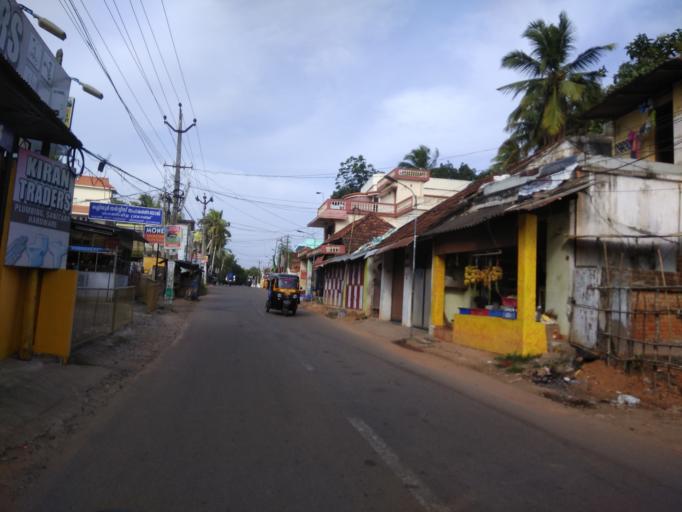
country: IN
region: Kerala
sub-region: Thiruvananthapuram
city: Thiruvananthapuram
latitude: 8.4516
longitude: 76.9980
